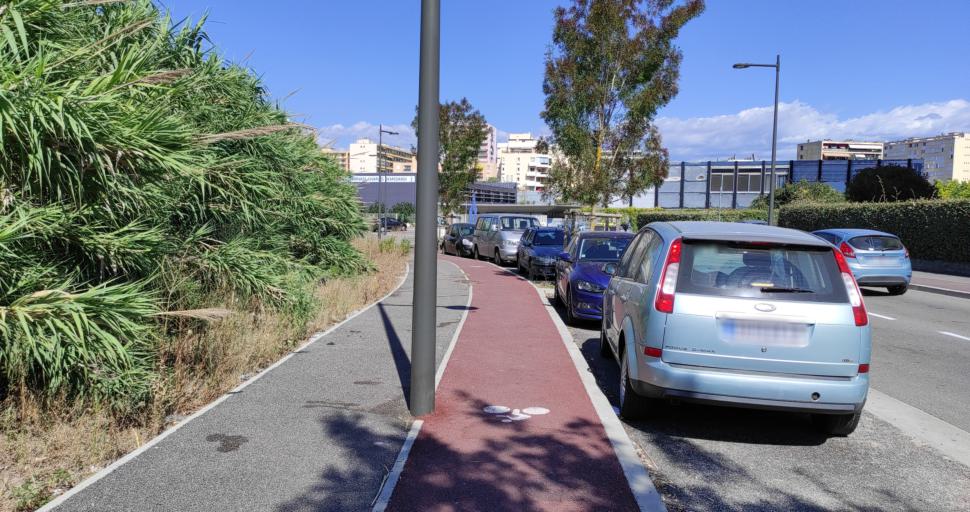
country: FR
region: Corsica
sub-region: Departement de la Corse-du-Sud
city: Ajaccio
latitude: 41.9355
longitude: 8.7368
